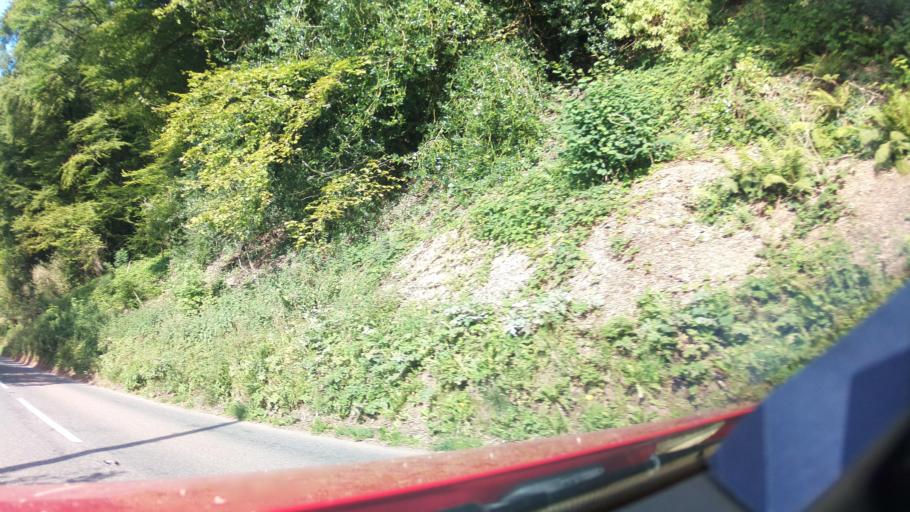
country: GB
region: England
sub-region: Devon
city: Tiverton
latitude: 50.8413
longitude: -3.5025
